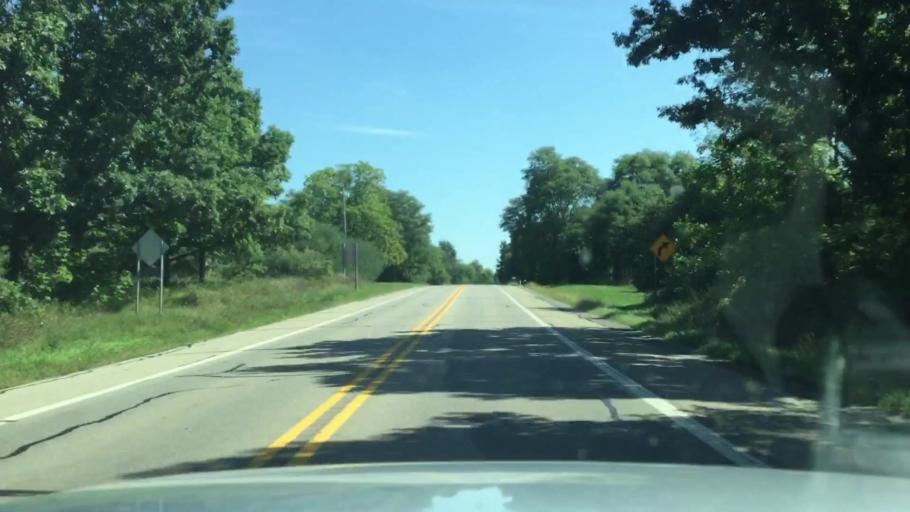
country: US
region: Michigan
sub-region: Jackson County
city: Brooklyn
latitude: 42.0600
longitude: -84.2122
